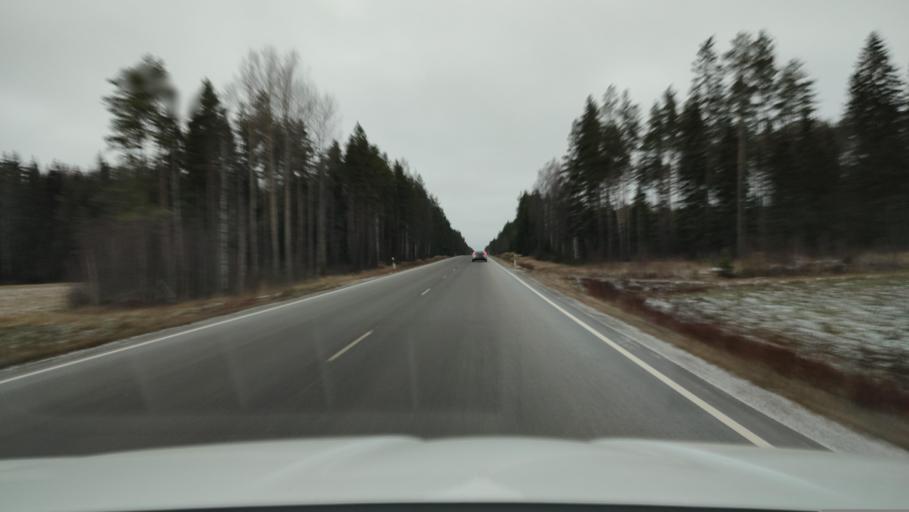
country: FI
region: Ostrobothnia
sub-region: Sydosterbotten
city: Naerpes
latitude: 62.5844
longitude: 21.4964
